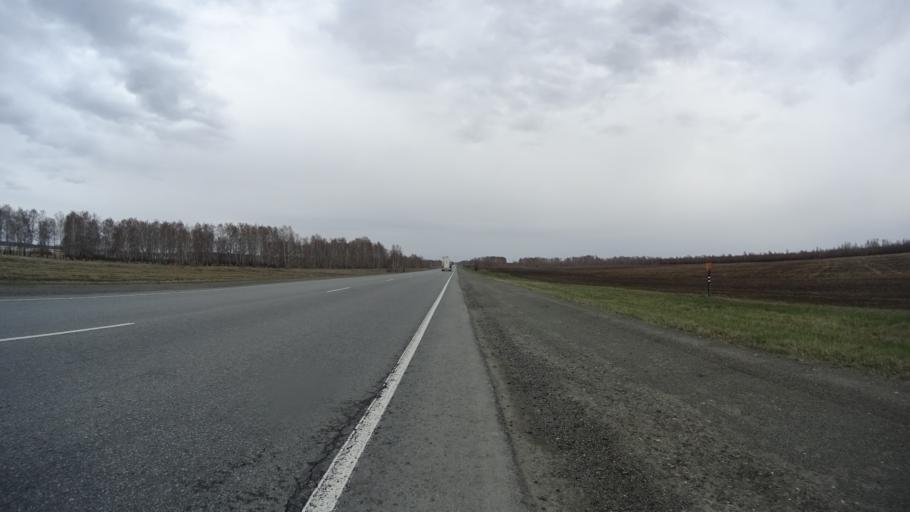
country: RU
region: Chelyabinsk
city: Krasnogorskiy
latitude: 54.6612
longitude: 61.2548
